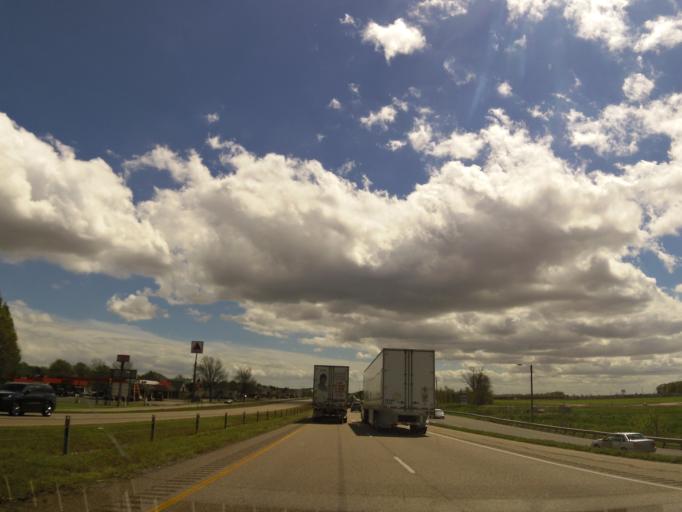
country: US
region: Arkansas
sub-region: Crittenden County
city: Marion
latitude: 35.2103
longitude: -90.2062
